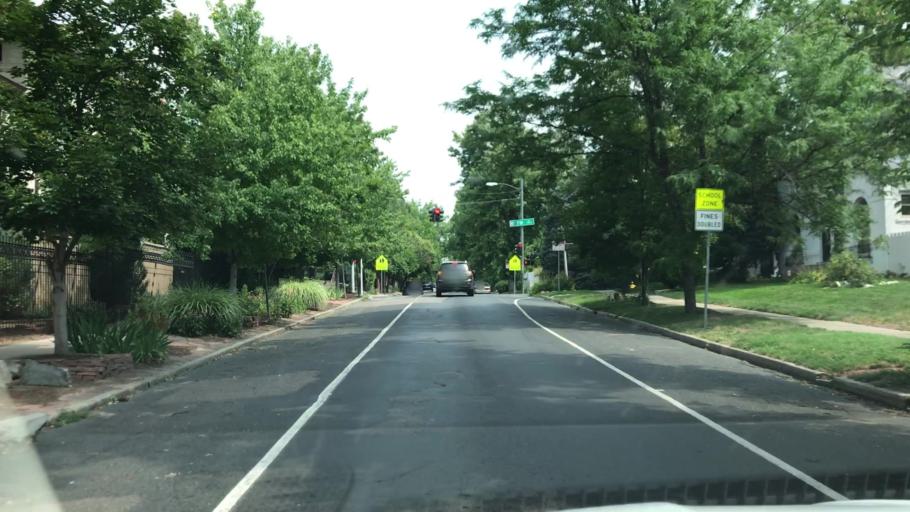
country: US
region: Colorado
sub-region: Denver County
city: Denver
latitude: 39.7268
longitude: -104.9729
